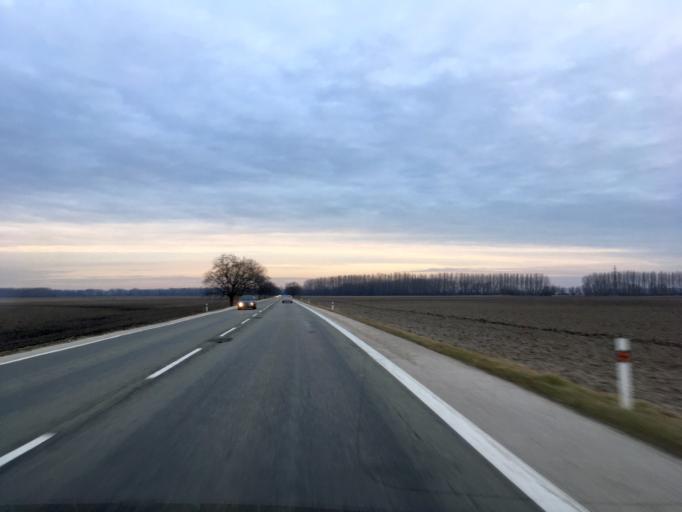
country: SK
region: Trnavsky
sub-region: Okres Dunajska Streda
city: Velky Meder
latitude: 47.9148
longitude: 17.7291
